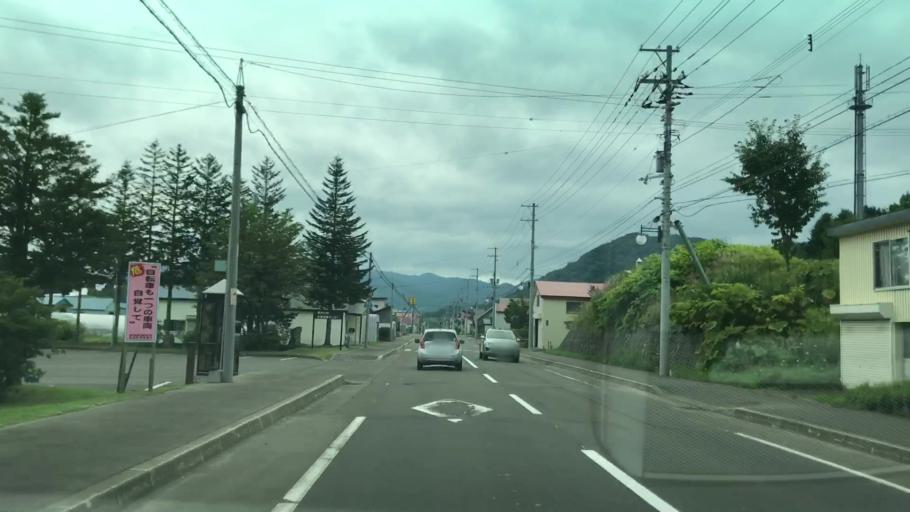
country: JP
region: Hokkaido
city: Yoichi
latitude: 43.0872
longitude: 140.8155
